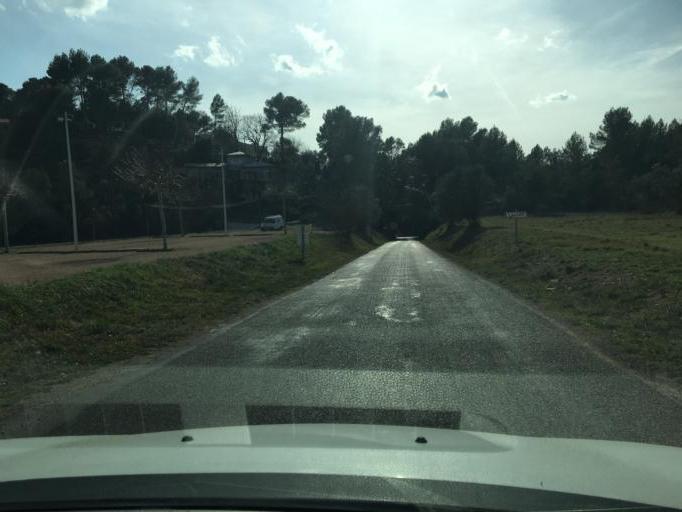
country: FR
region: Provence-Alpes-Cote d'Azur
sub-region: Departement du Var
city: Callas
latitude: 43.5900
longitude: 6.5296
